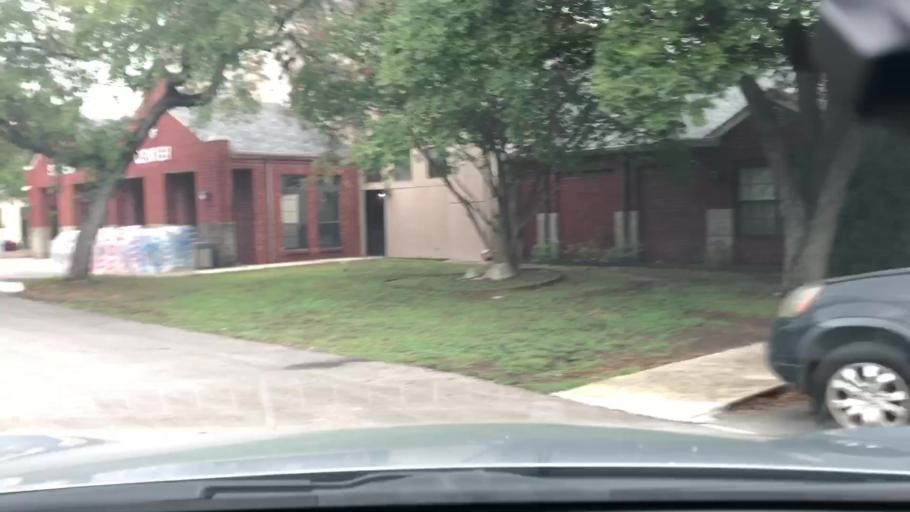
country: US
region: Texas
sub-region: Bexar County
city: Leon Valley
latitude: 29.4740
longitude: -98.6703
